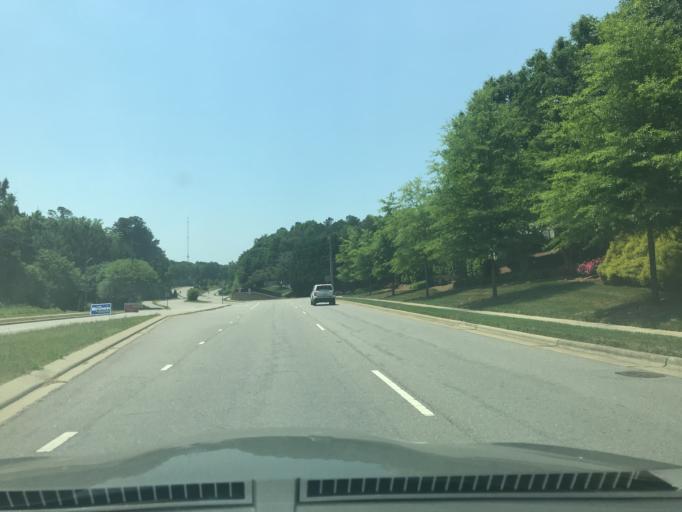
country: US
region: North Carolina
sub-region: Wake County
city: Cary
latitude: 35.7967
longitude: -78.7271
